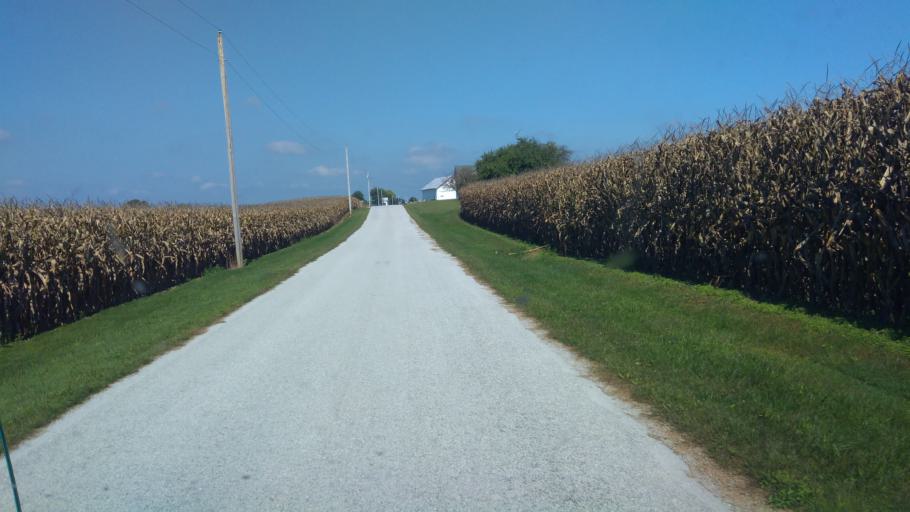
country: US
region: Ohio
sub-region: Hardin County
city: Kenton
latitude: 40.6984
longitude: -83.6014
